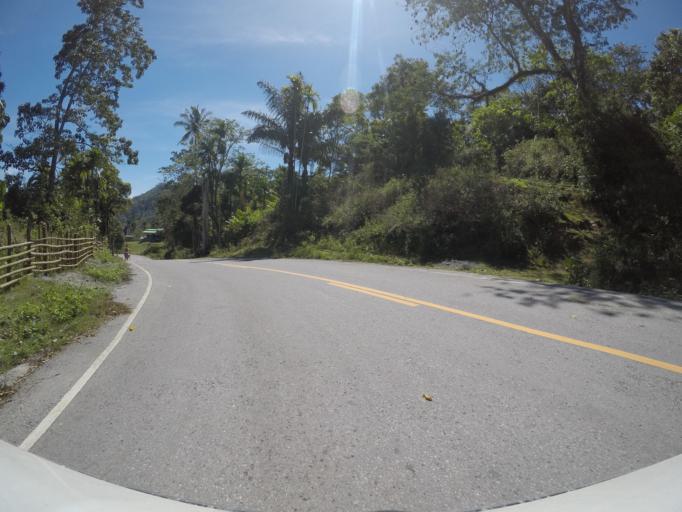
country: TL
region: Manufahi
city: Same
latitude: -8.9108
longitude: 125.9743
